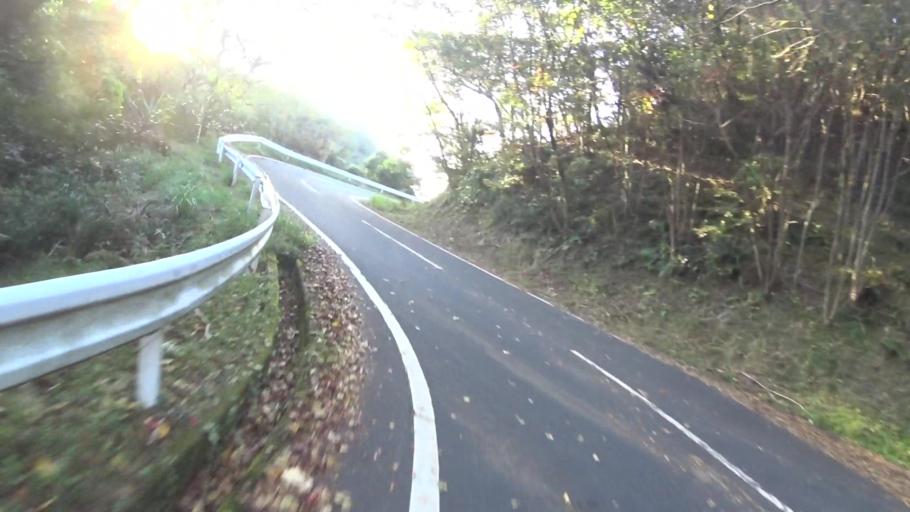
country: JP
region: Hyogo
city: Toyooka
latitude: 35.6878
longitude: 134.9883
